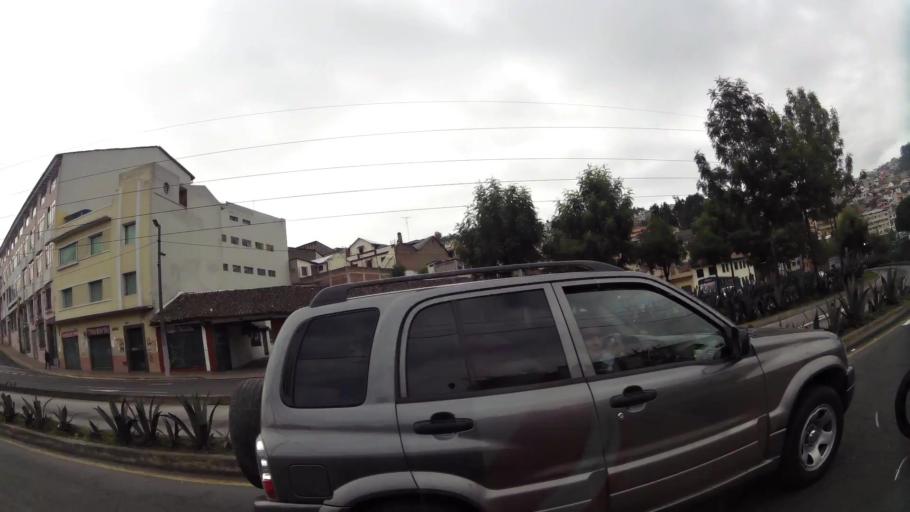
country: EC
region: Pichincha
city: Quito
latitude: -0.2236
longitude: -78.5079
